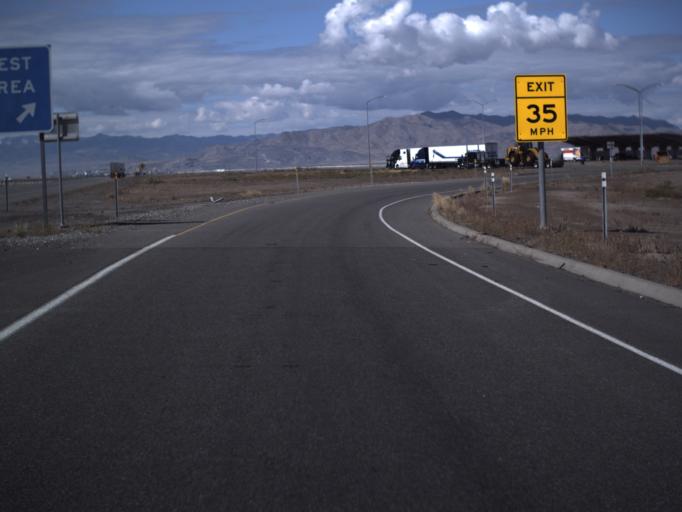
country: US
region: Utah
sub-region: Tooele County
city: Wendover
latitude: 40.7395
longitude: -113.8495
